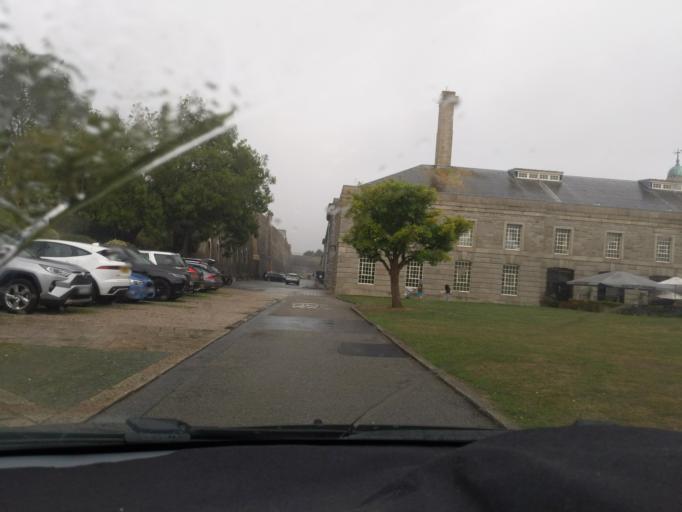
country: GB
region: England
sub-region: Cornwall
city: Millbrook
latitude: 50.3616
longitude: -4.1631
